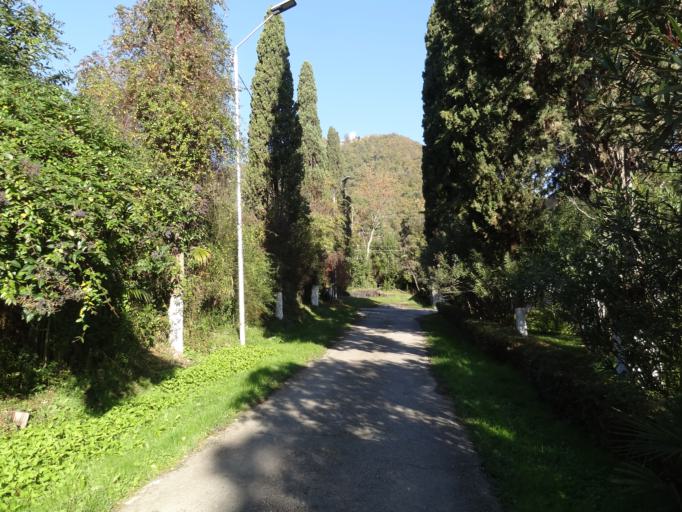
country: GE
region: Abkhazia
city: Stantsiya Novyy Afon
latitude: 43.0862
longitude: 40.8124
